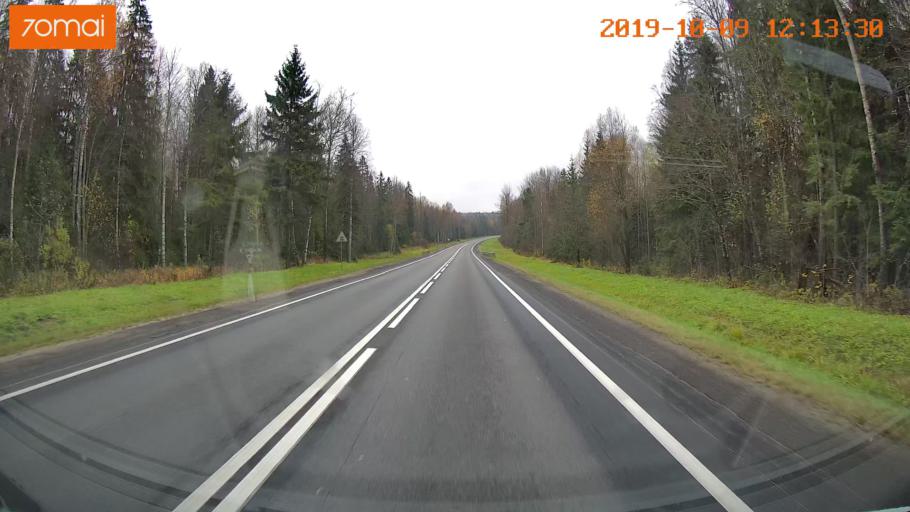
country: RU
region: Jaroslavl
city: Prechistoye
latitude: 58.5097
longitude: 40.3454
